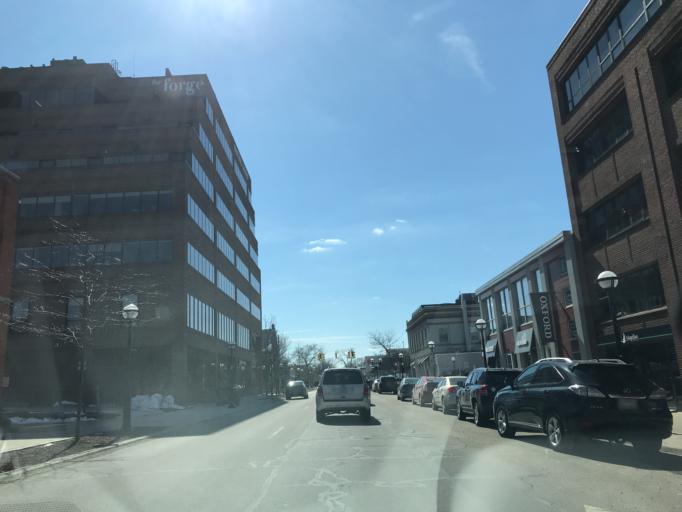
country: US
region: Michigan
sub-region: Washtenaw County
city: Ann Arbor
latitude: 42.2804
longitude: -83.7461
